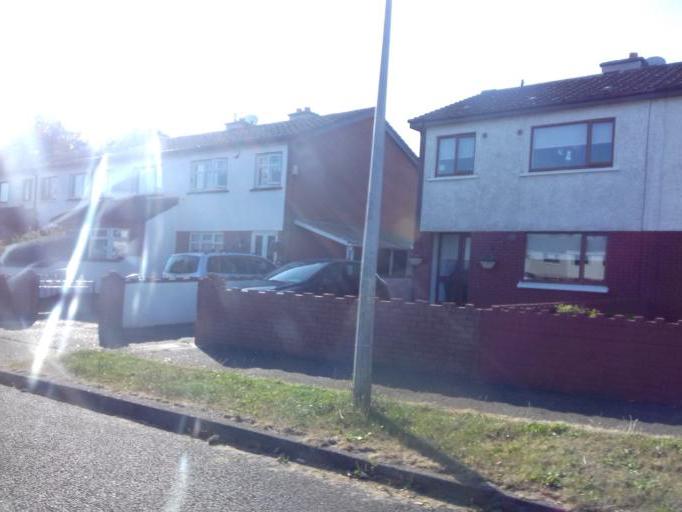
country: IE
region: Leinster
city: Ballymun
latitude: 53.4537
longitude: -6.2892
